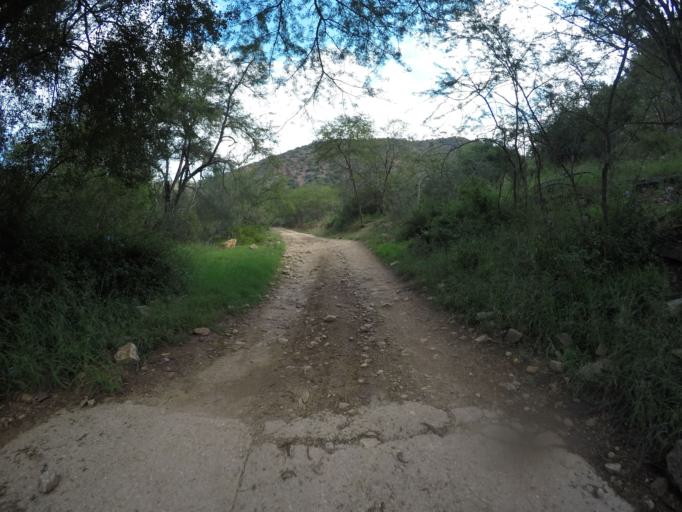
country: ZA
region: Eastern Cape
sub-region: Cacadu District Municipality
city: Kareedouw
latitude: -33.6365
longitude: 24.3173
